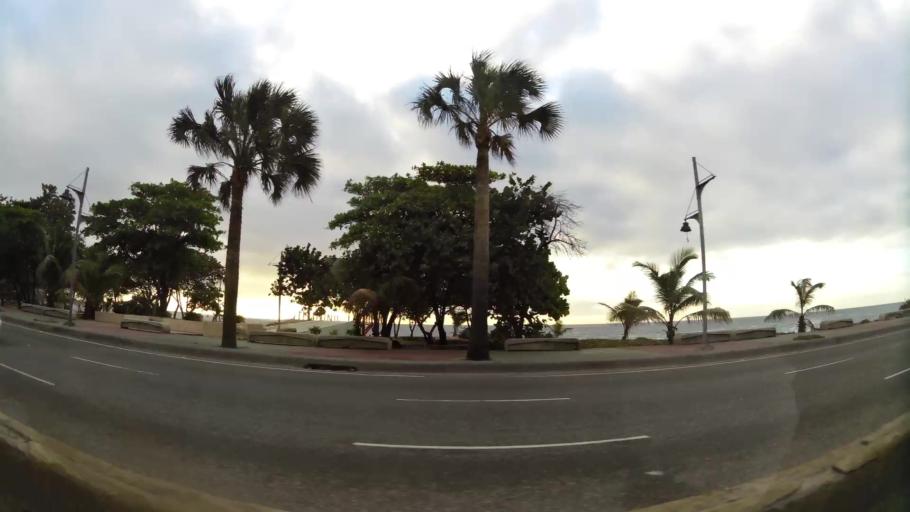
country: DO
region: Nacional
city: La Julia
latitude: 18.4510
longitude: -69.9223
